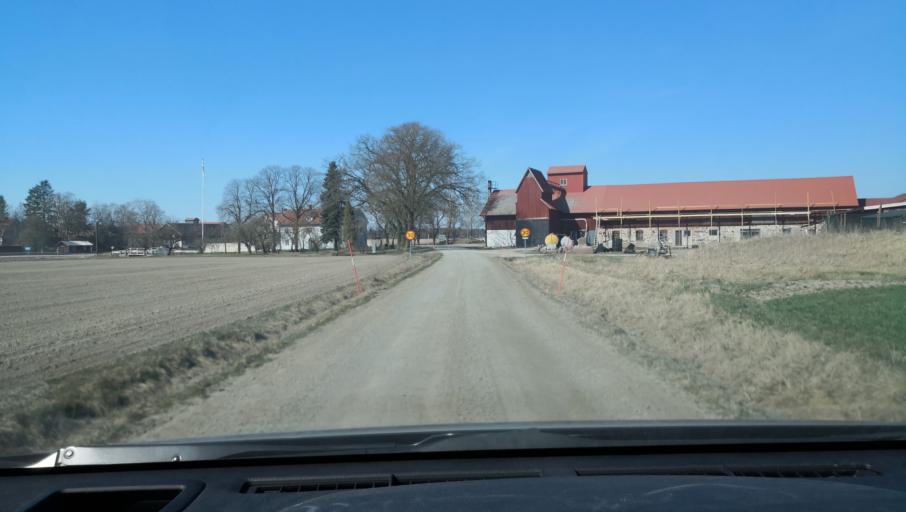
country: SE
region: Vaestmanland
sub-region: Sala Kommun
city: Sala
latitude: 59.8557
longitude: 16.5393
